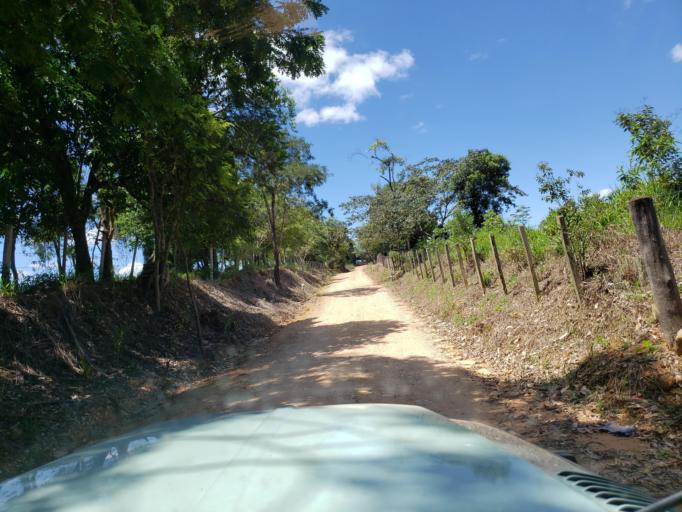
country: BR
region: Sao Paulo
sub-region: Moji-Guacu
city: Mogi-Gaucu
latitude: -22.3159
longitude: -46.8797
